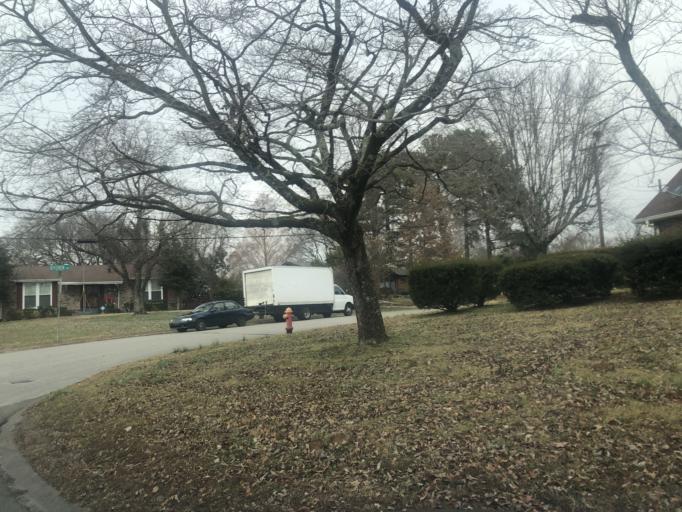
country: US
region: Tennessee
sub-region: Rutherford County
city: La Vergne
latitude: 36.0808
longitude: -86.6410
